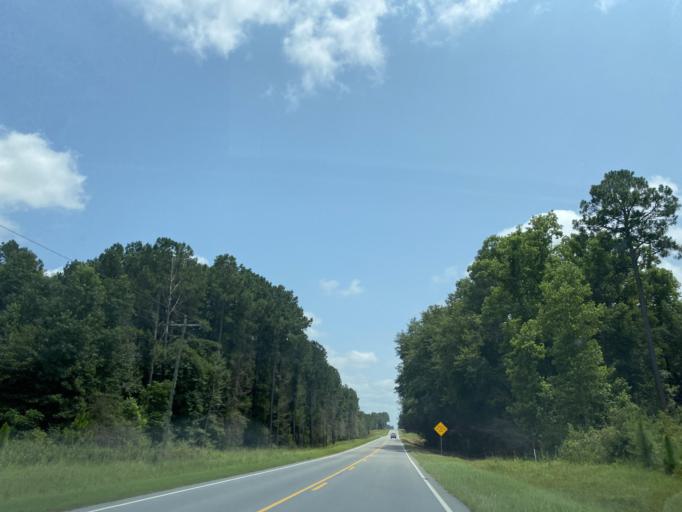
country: US
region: Georgia
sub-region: Jeff Davis County
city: Hazlehurst
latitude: 31.7630
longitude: -82.5547
